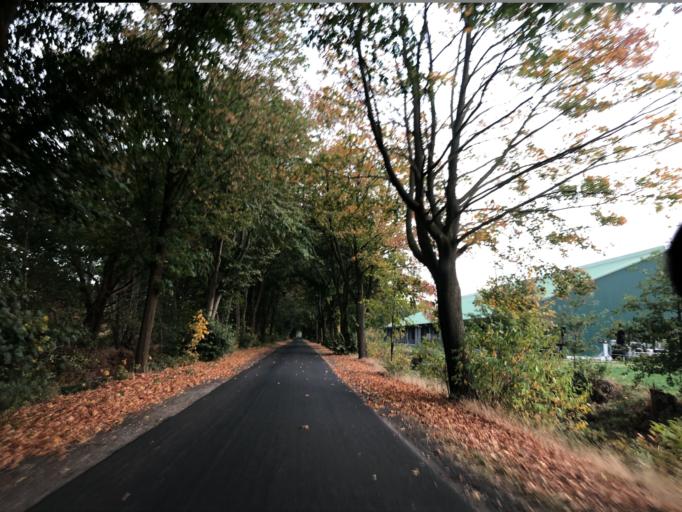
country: DE
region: Lower Saxony
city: Papenburg
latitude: 53.0511
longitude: 7.4244
